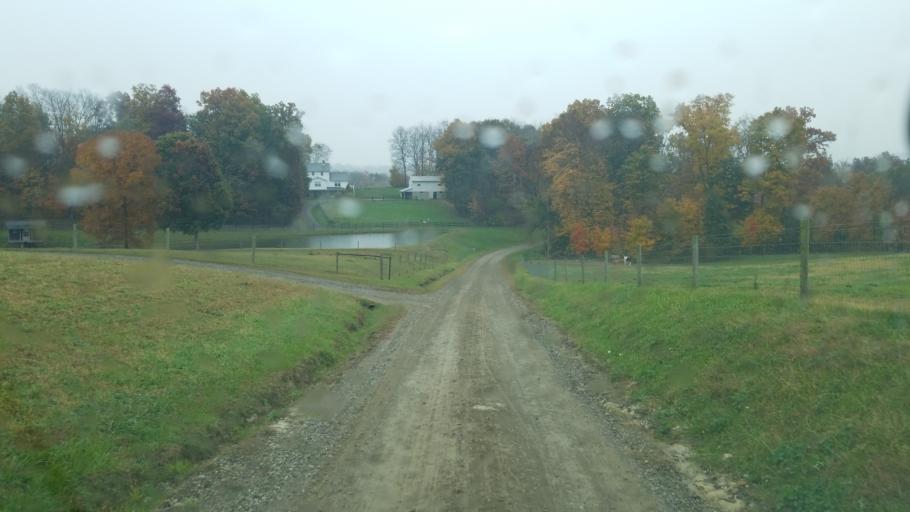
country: US
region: Ohio
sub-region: Holmes County
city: Millersburg
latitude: 40.4407
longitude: -81.8173
